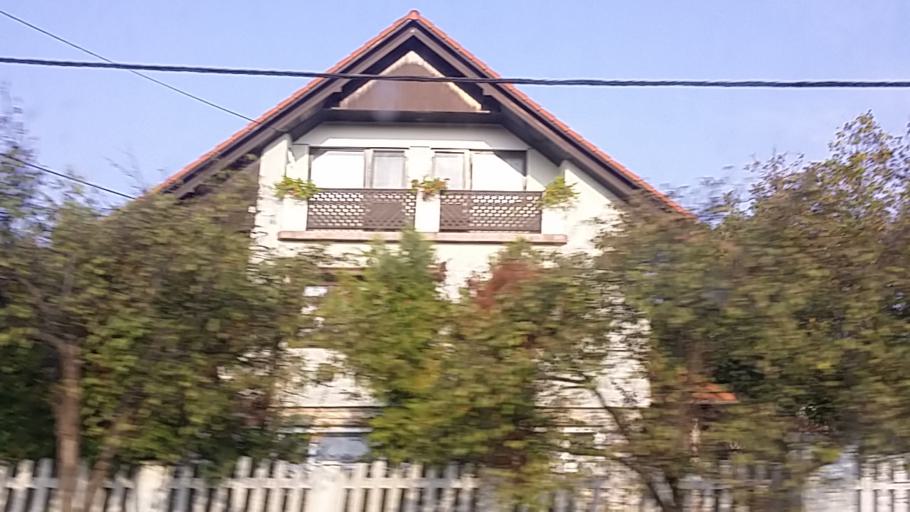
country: HU
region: Pest
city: Pilisvorosvar
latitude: 47.6330
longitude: 18.8997
